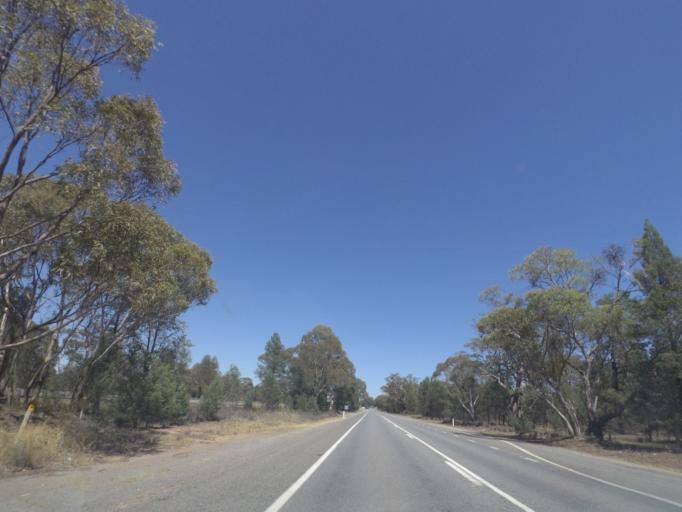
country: AU
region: New South Wales
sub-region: Narrandera
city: Narrandera
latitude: -34.7383
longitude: 146.5786
